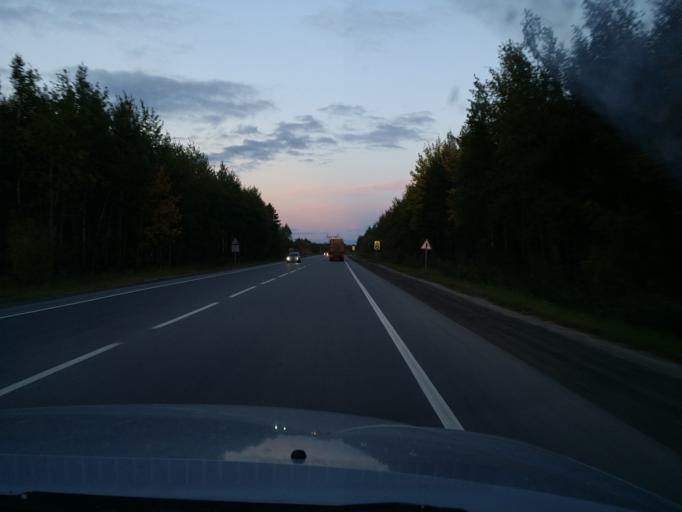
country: RU
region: Khanty-Mansiyskiy Avtonomnyy Okrug
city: Megion
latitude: 61.0516
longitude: 76.3264
